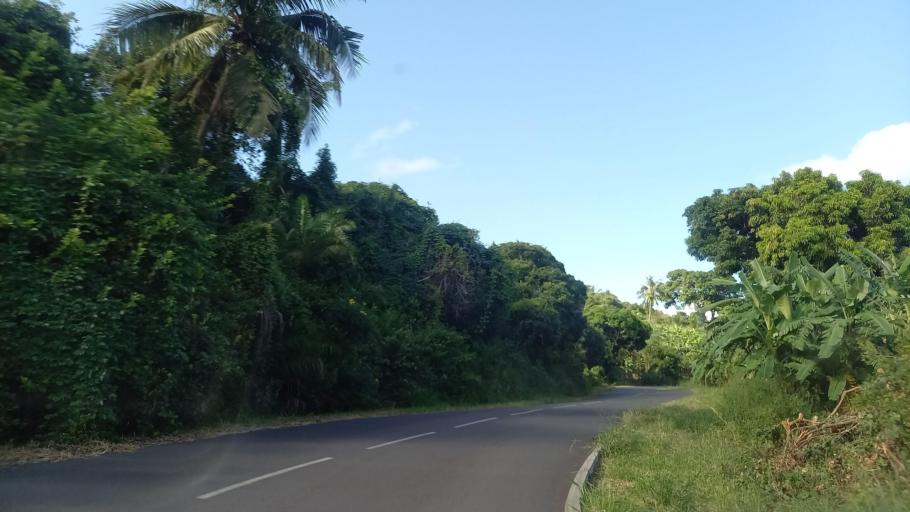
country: YT
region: Kani-Keli
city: Kani Keli
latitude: -12.9690
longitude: 45.1116
